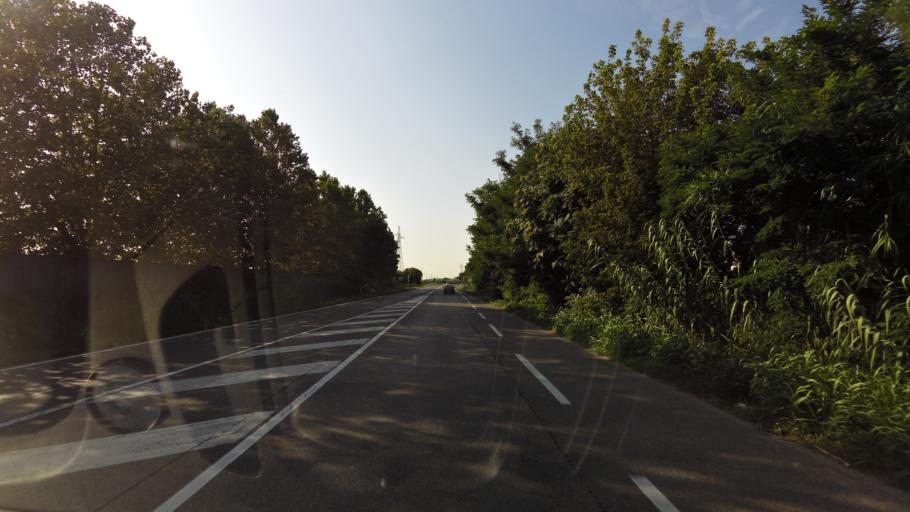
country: IT
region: Emilia-Romagna
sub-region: Provincia di Ravenna
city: Cervia
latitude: 44.2383
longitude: 12.3561
